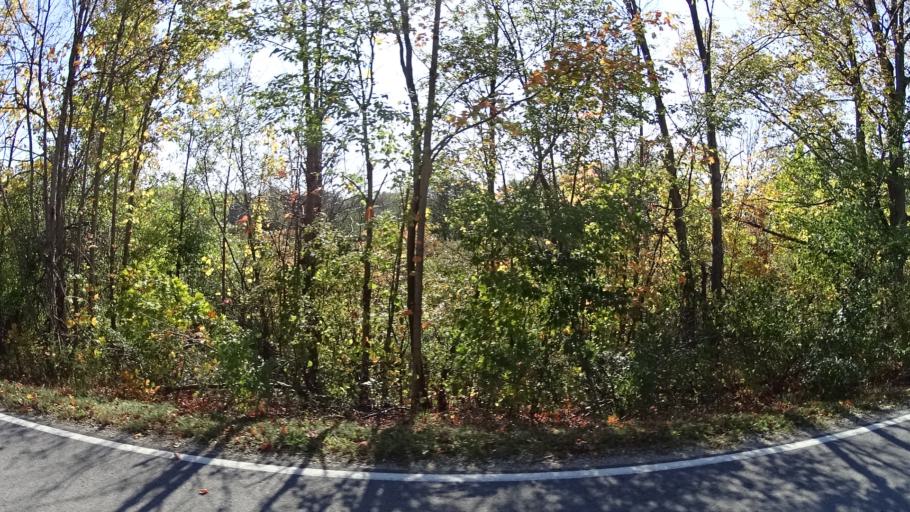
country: US
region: Ohio
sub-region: Lorain County
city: Vermilion-on-the-Lake
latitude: 41.4009
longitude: -82.3082
